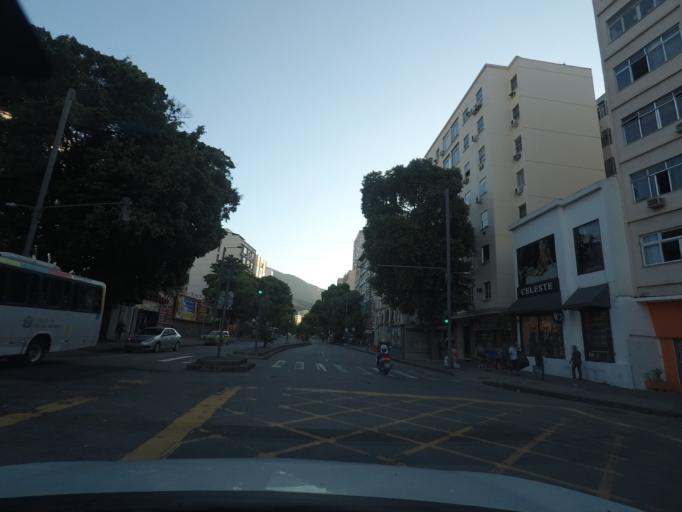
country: BR
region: Rio de Janeiro
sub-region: Rio De Janeiro
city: Rio de Janeiro
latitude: -22.9263
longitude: -43.2352
